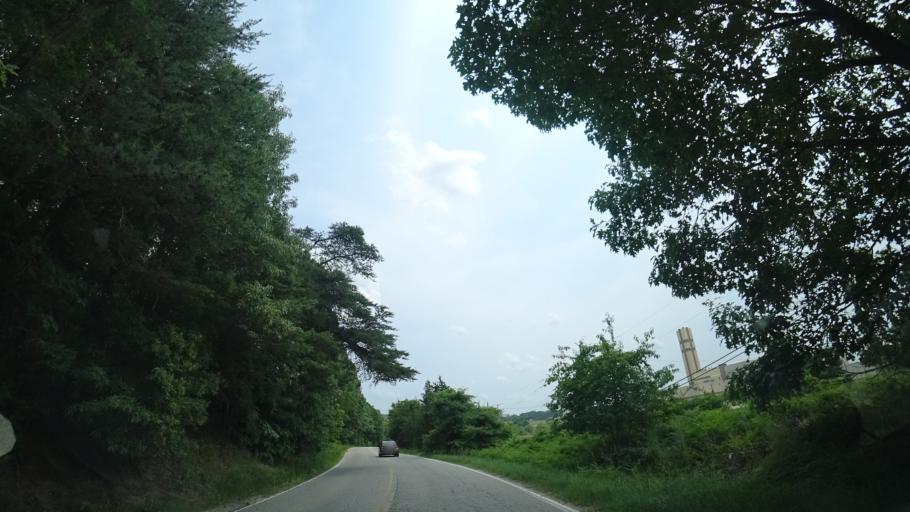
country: US
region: Virginia
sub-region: Fairfax County
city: Lorton
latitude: 38.6992
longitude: -77.2395
